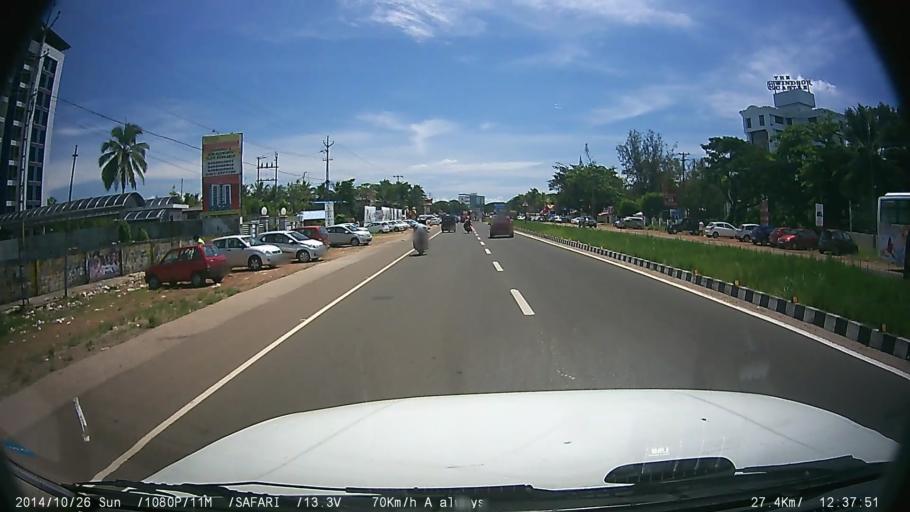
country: IN
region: Kerala
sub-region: Kottayam
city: Kottayam
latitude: 9.5730
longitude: 76.5197
